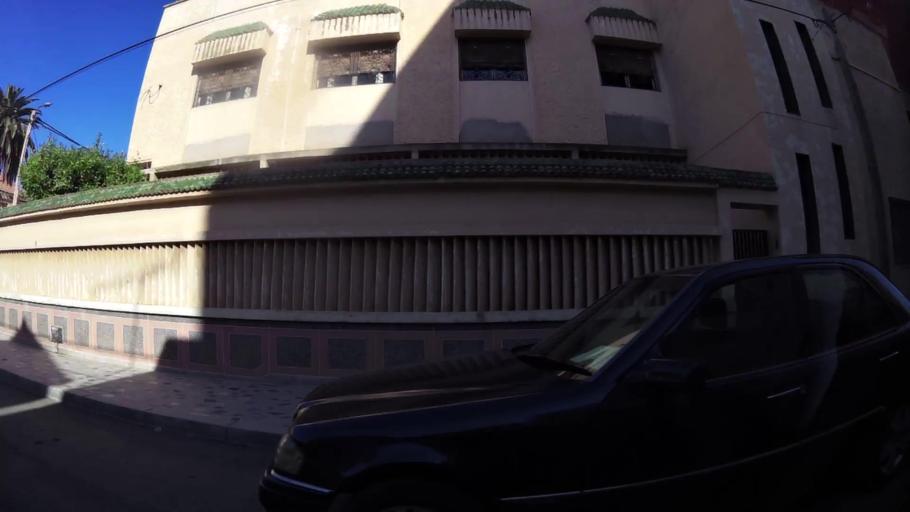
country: MA
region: Oriental
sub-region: Oujda-Angad
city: Oujda
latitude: 34.6837
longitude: -1.9200
